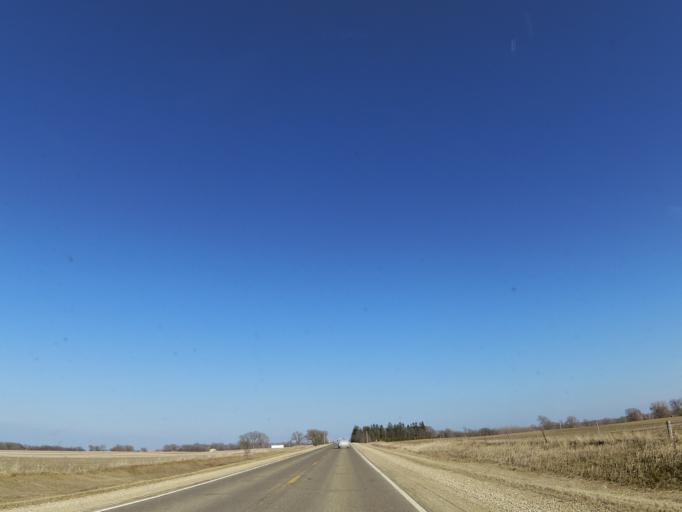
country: US
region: Iowa
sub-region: Worth County
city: Northwood
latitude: 43.4443
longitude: -93.2803
